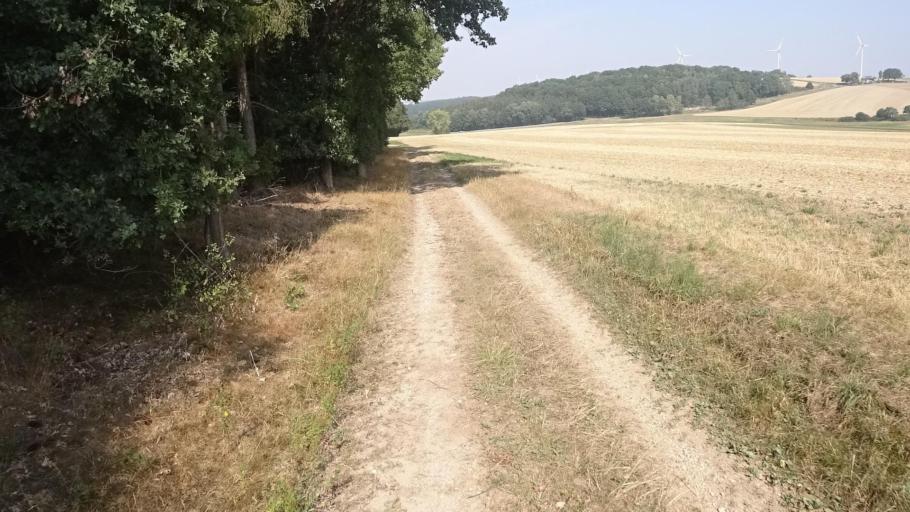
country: DE
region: Rheinland-Pfalz
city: Wahlbach
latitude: 49.9915
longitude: 7.5937
